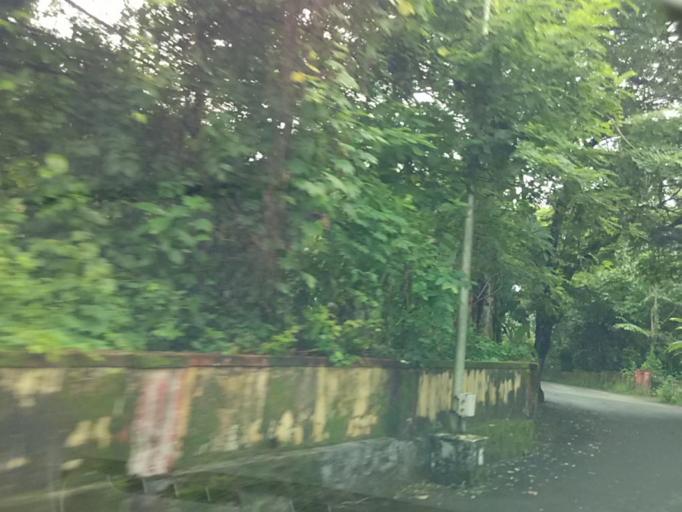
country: IN
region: Kerala
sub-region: Kozhikode
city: Mavoor
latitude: 11.3188
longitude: 75.9321
